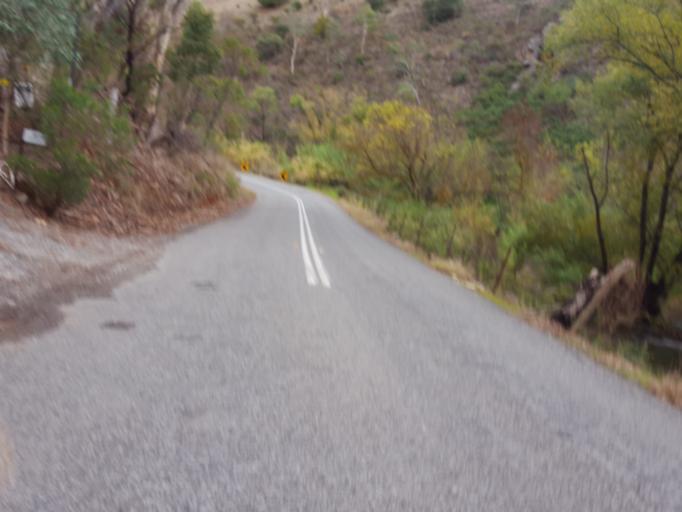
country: AU
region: South Australia
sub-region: Campbelltown
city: Athelstone
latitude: -34.8728
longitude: 138.7548
